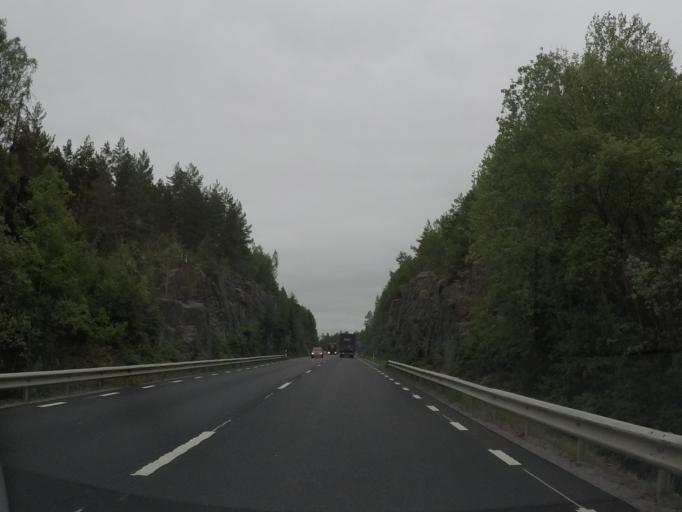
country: SE
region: Soedermanland
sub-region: Flens Kommun
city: Flen
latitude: 59.0684
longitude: 16.6186
